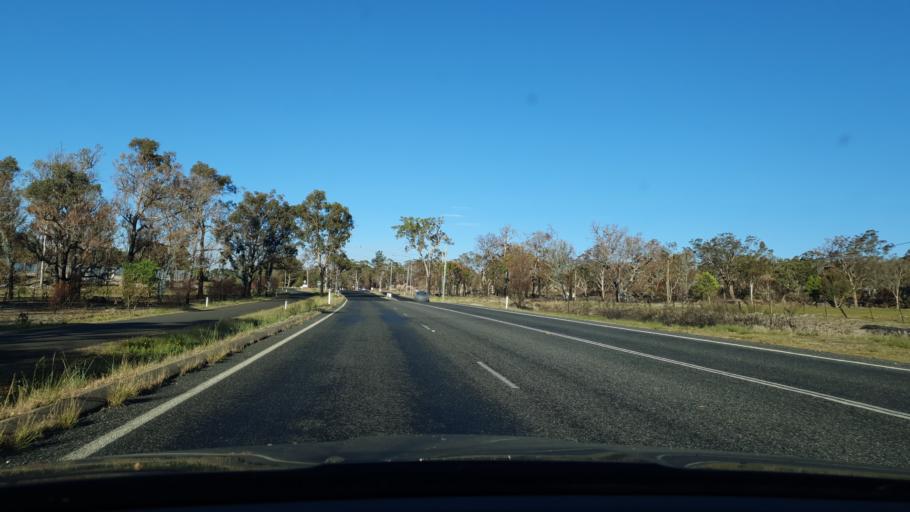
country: AU
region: Queensland
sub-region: Southern Downs
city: Stanthorpe
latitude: -28.6370
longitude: 151.9485
